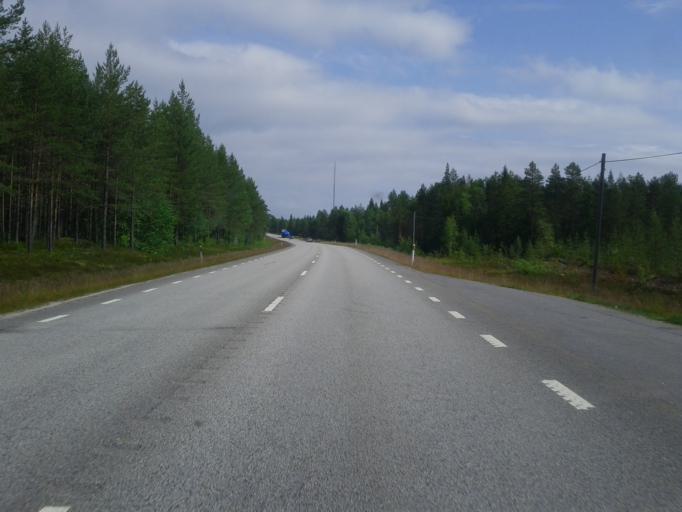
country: SE
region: Vaesterbotten
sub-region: Robertsfors Kommun
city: Robertsfors
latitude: 64.1861
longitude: 20.9933
